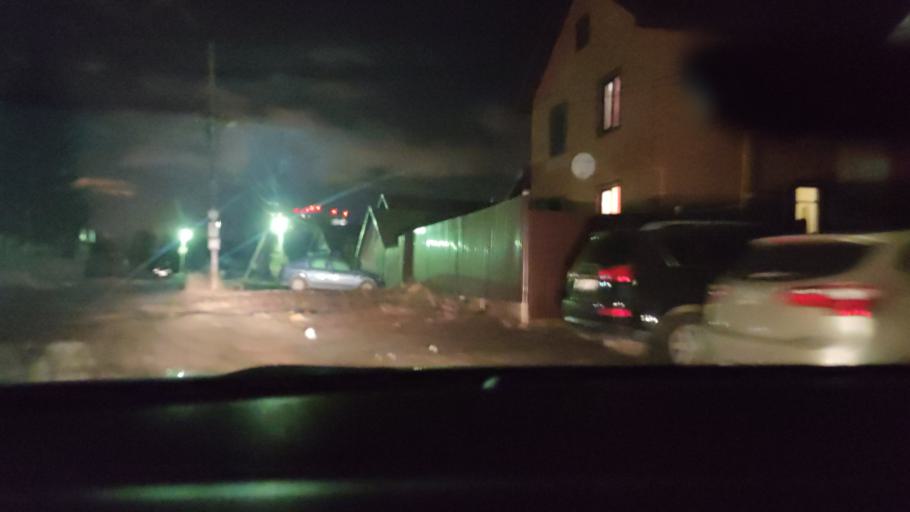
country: RU
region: Tatarstan
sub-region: Gorod Kazan'
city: Kazan
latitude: 55.8012
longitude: 49.2303
